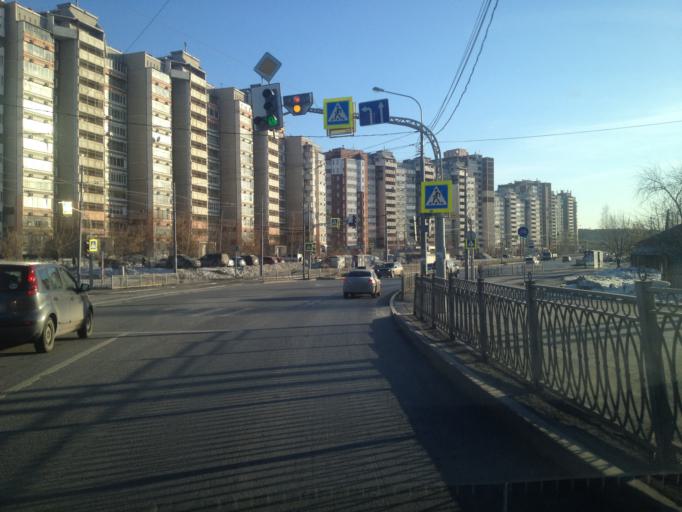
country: RU
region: Sverdlovsk
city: Sovkhoznyy
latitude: 56.8248
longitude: 60.5433
